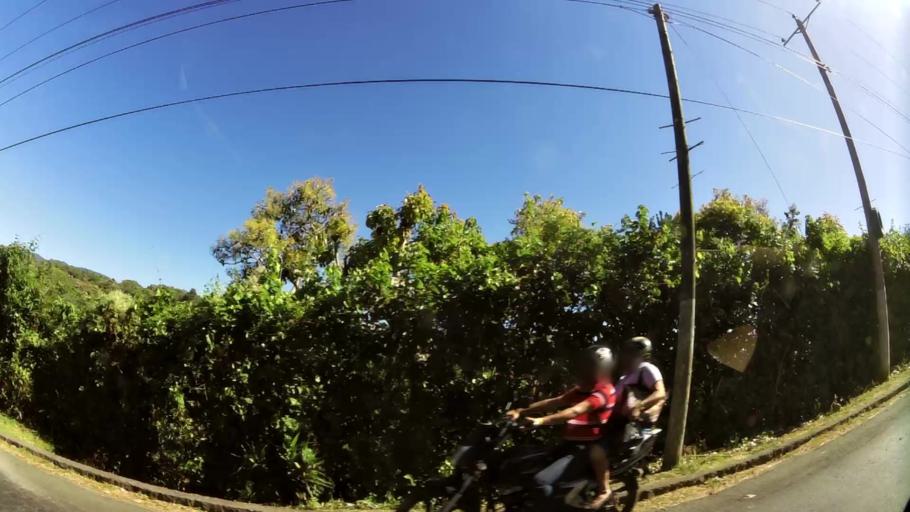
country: SV
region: Sonsonate
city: Juayua
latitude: 13.8340
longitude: -89.7543
